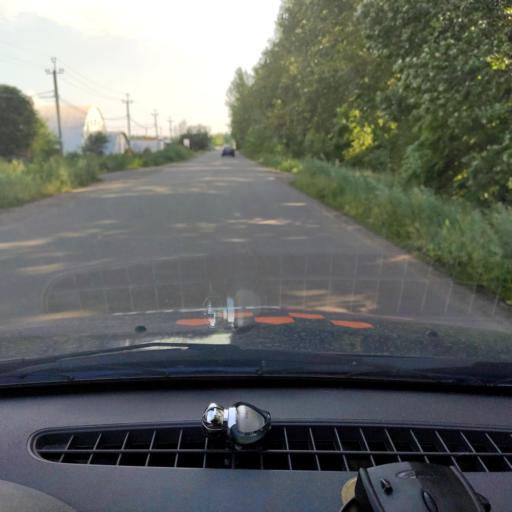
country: RU
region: Voronezj
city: Podkletnoye
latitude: 51.6034
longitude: 39.4291
